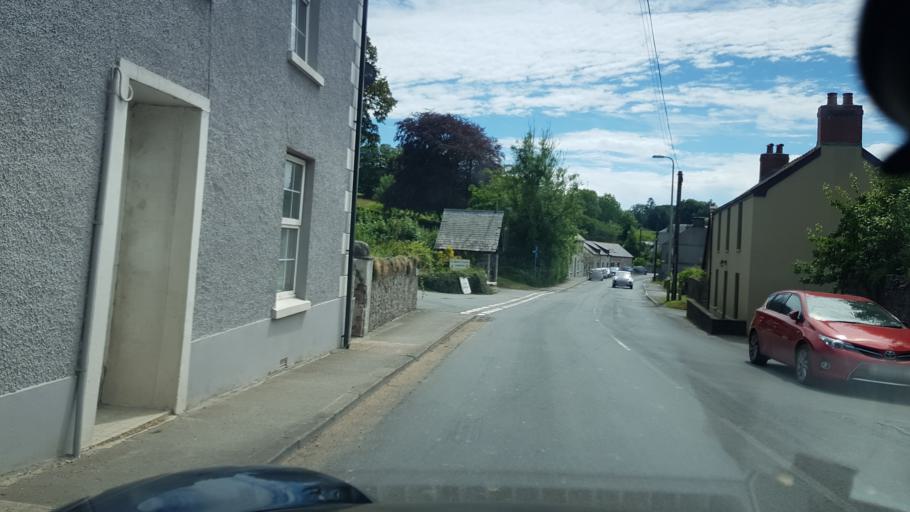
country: GB
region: Wales
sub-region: Carmarthenshire
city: Saint Clears
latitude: 51.7754
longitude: -4.4639
